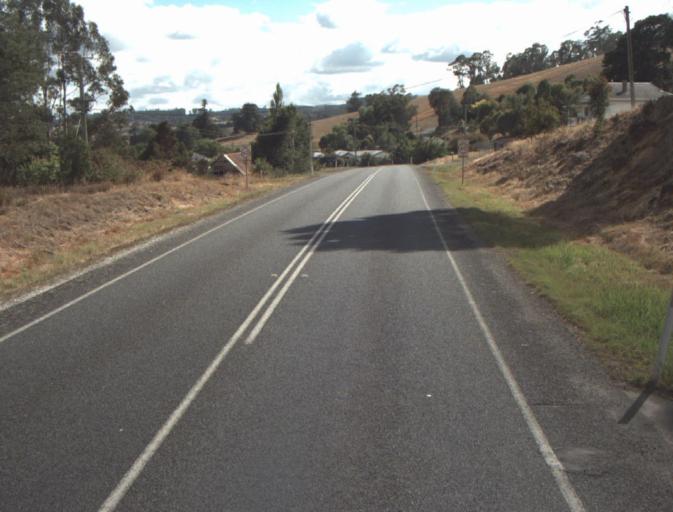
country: AU
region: Tasmania
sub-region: Launceston
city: Mayfield
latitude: -41.2641
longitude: 147.2163
